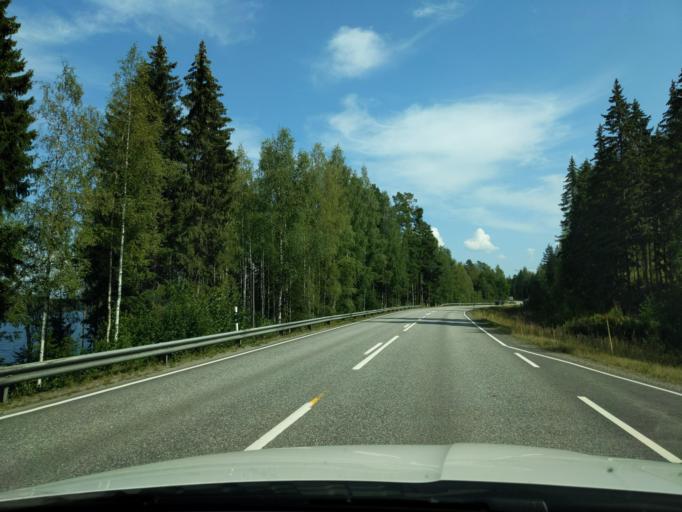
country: FI
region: Paijanne Tavastia
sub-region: Lahti
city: Padasjoki
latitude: 61.3275
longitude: 25.1858
